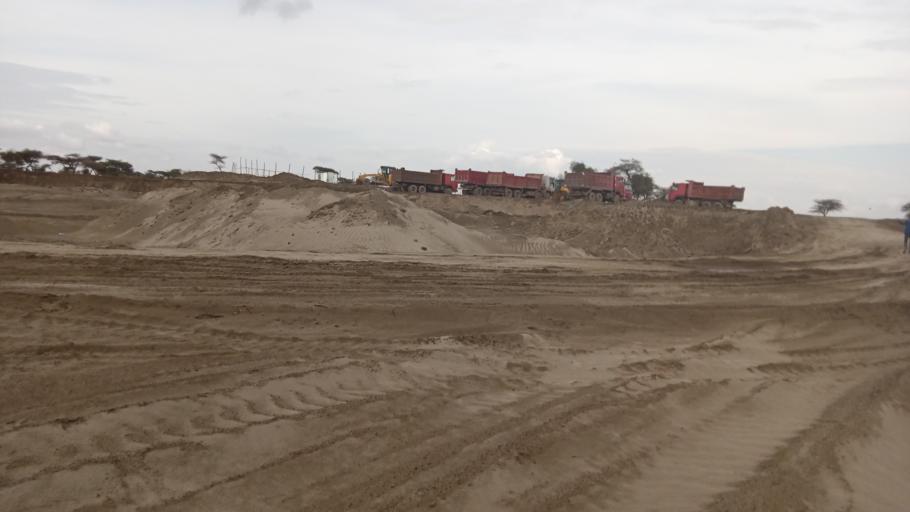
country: ET
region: Oromiya
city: Ziway
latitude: 7.9203
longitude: 38.6817
